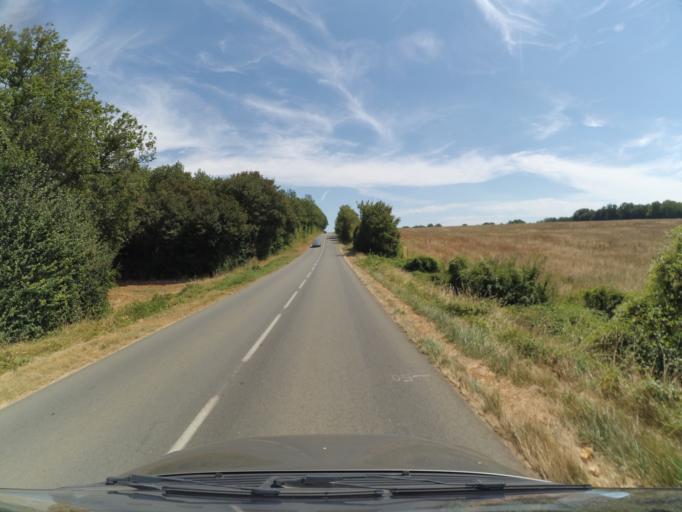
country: FR
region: Poitou-Charentes
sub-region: Departement de la Vienne
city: Saint-Maurice-la-Clouere
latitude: 46.3941
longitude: 0.3806
